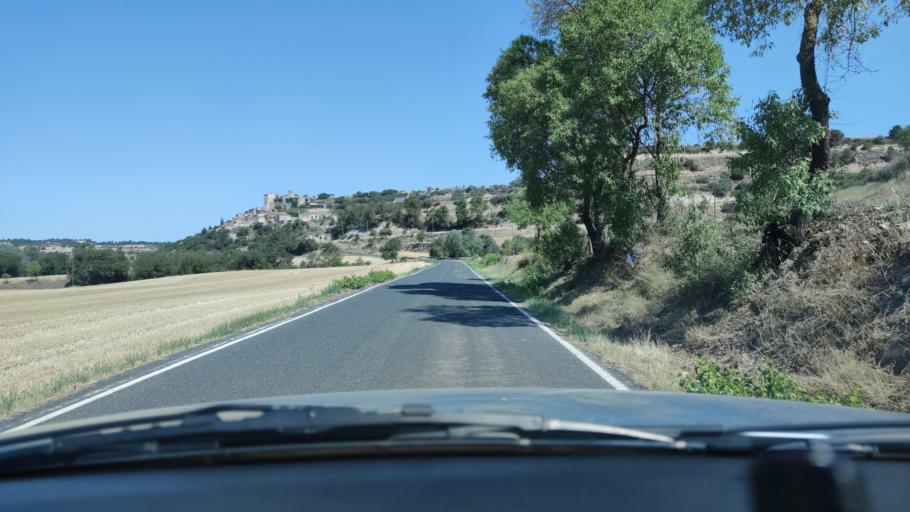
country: ES
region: Catalonia
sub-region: Provincia de Lleida
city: Sant Guim de Freixenet
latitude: 41.6722
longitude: 1.3617
